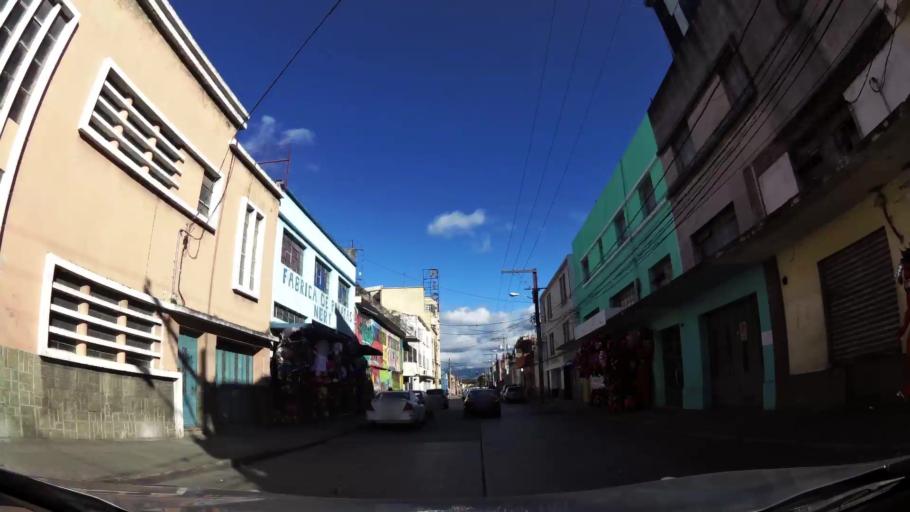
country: GT
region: Guatemala
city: Guatemala City
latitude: 14.6394
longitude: -90.5070
